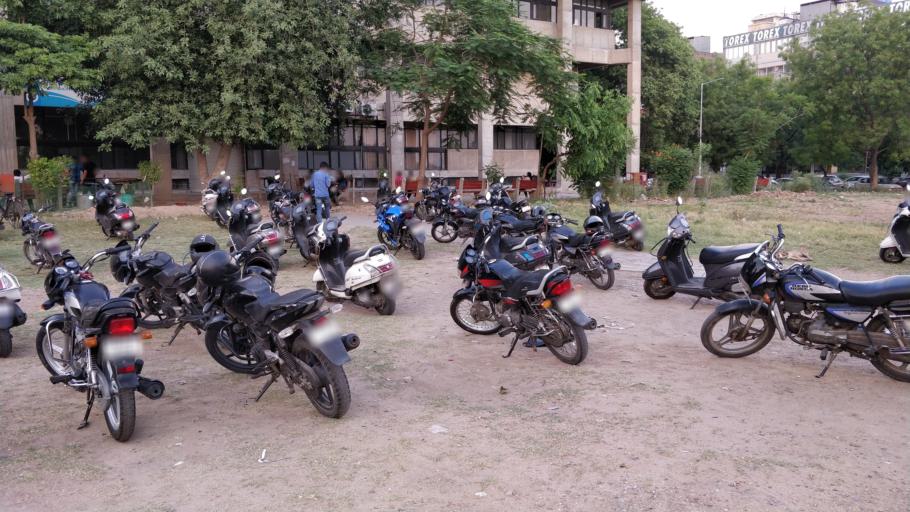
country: IN
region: Chandigarh
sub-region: Chandigarh
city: Chandigarh
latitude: 30.7200
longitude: 76.7670
